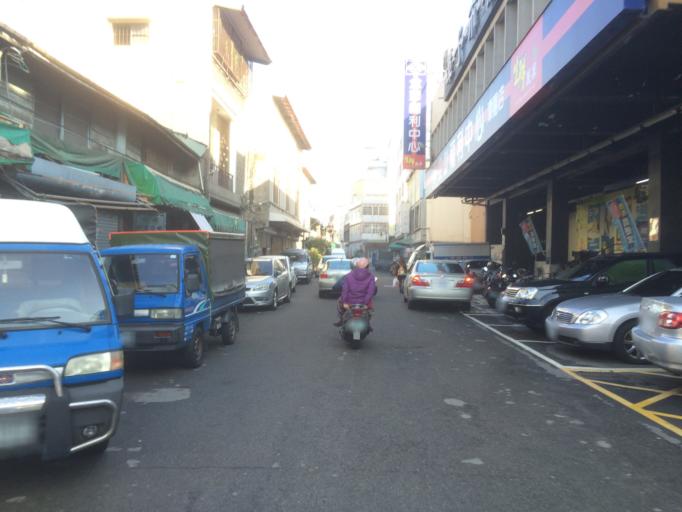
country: TW
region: Taiwan
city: Fengyuan
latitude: 24.2118
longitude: 120.7063
